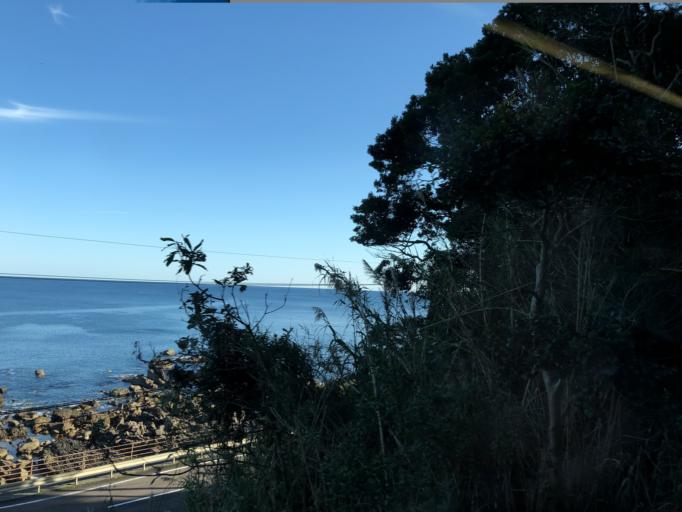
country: JP
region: Kochi
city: Nakamura
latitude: 33.0516
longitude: 133.0975
